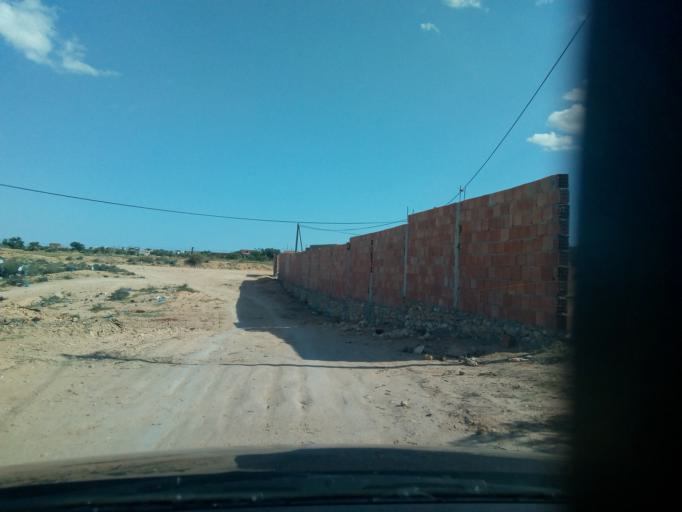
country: TN
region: Safaqis
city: Sfax
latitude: 34.7267
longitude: 10.6044
